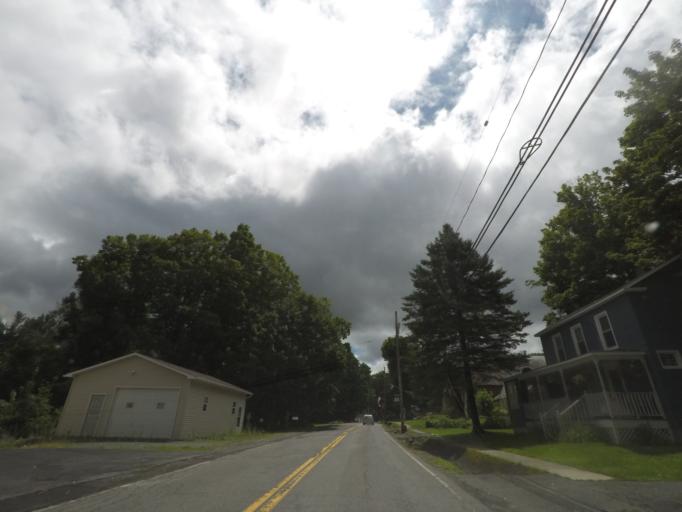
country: US
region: Massachusetts
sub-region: Berkshire County
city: Williamstown
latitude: 42.6954
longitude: -73.3744
